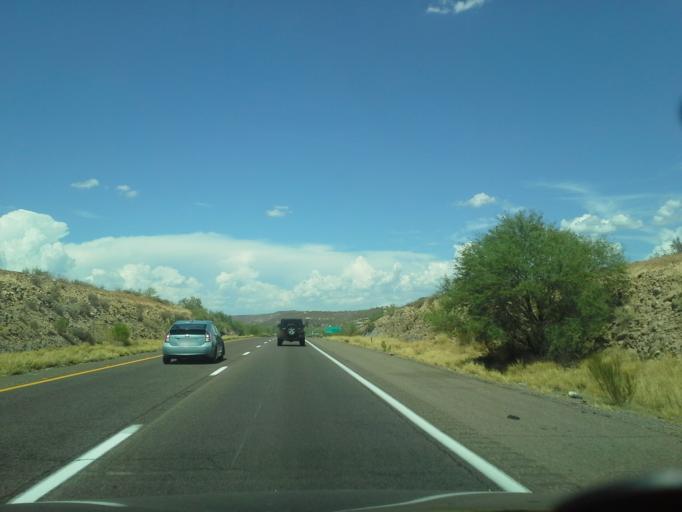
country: US
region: Arizona
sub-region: Maricopa County
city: New River
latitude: 33.9258
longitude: -112.1423
